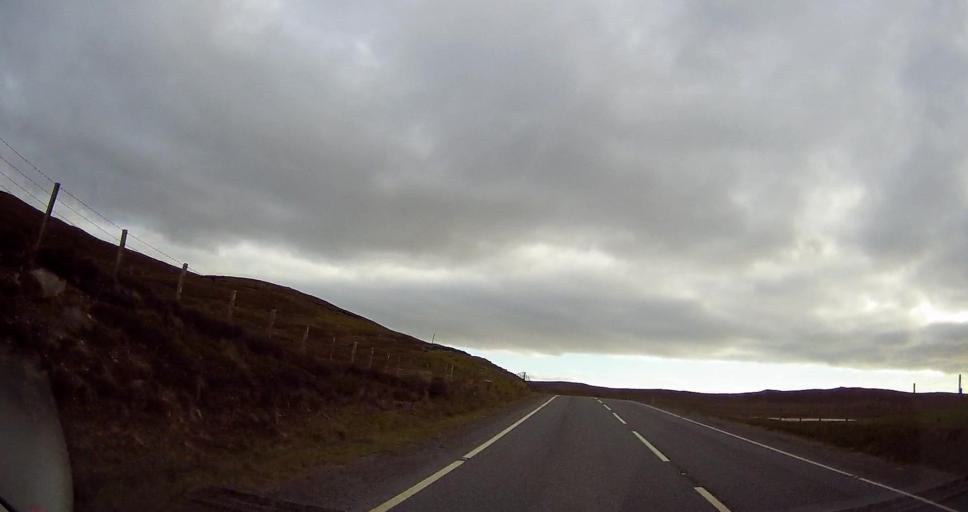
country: GB
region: Scotland
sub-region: Shetland Islands
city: Lerwick
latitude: 60.4285
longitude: -1.3051
